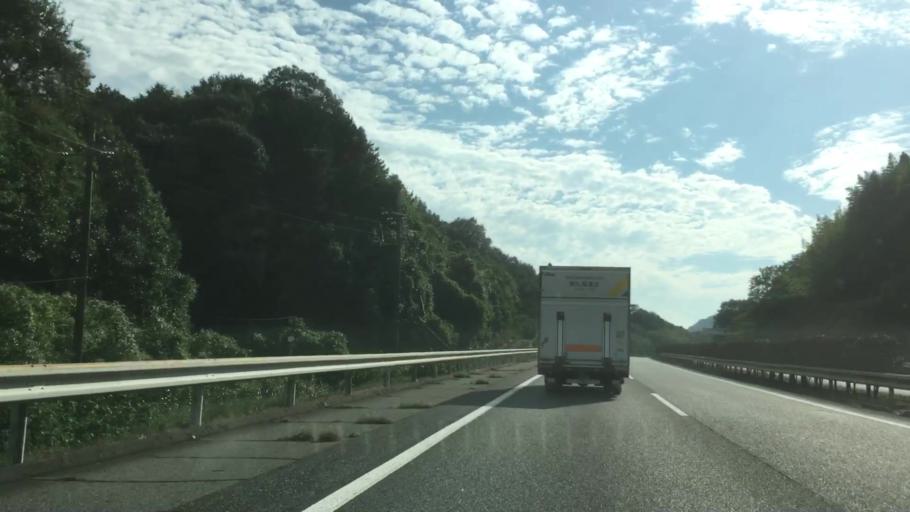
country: JP
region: Yamaguchi
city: Yanai
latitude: 34.0739
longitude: 132.0677
